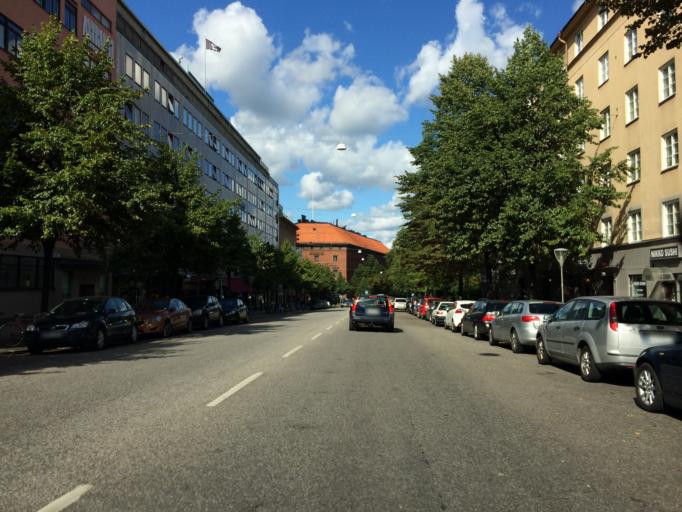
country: SE
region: Stockholm
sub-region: Stockholms Kommun
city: Stockholm
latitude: 59.3460
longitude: 18.0400
